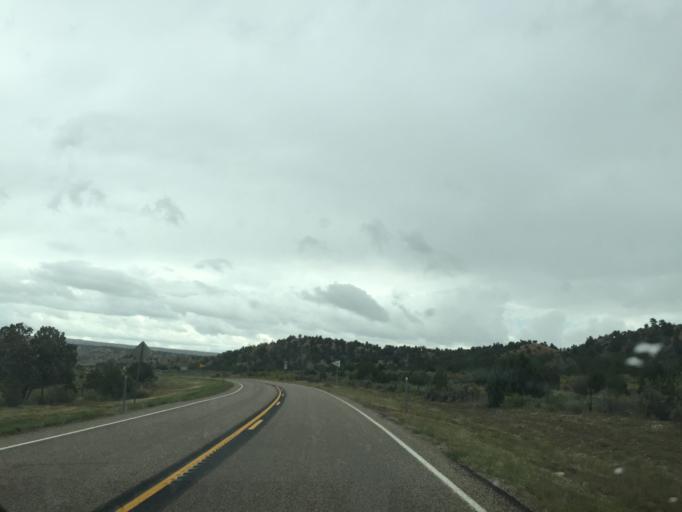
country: US
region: Utah
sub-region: Garfield County
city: Panguitch
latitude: 37.6151
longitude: -112.0754
